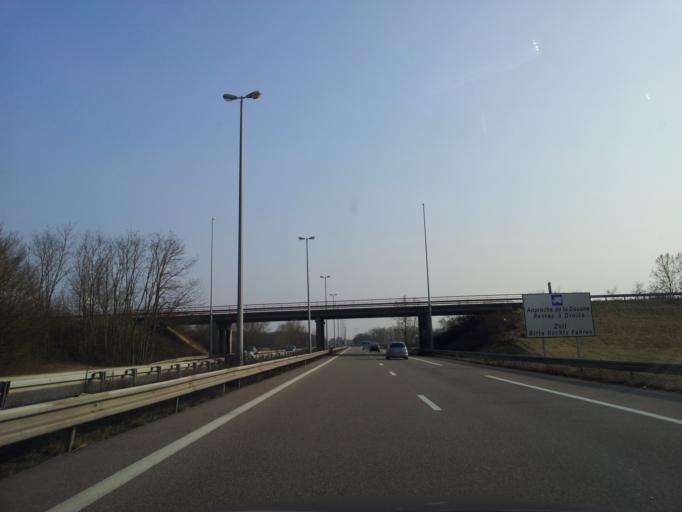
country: FR
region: Alsace
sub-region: Departement du Haut-Rhin
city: Bartenheim
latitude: 47.6371
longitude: 7.5000
